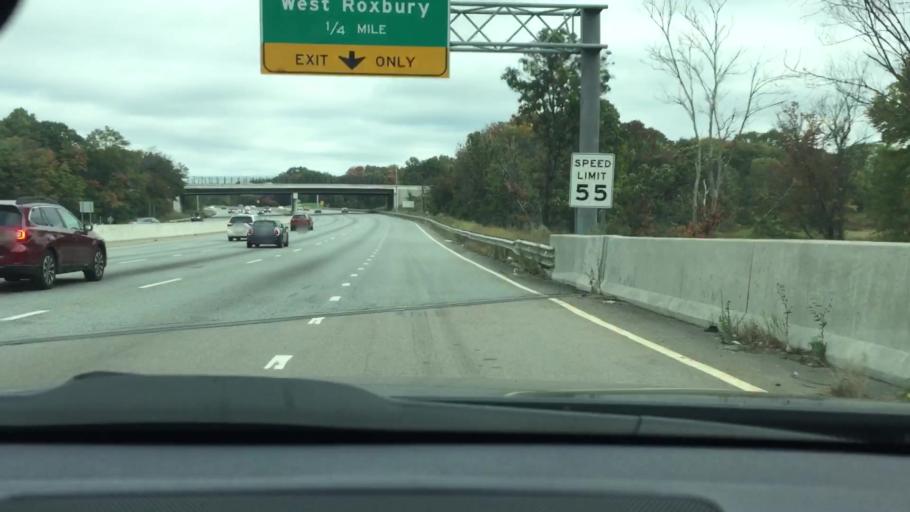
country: US
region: Massachusetts
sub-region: Norfolk County
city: Needham
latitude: 42.2677
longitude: -71.2020
